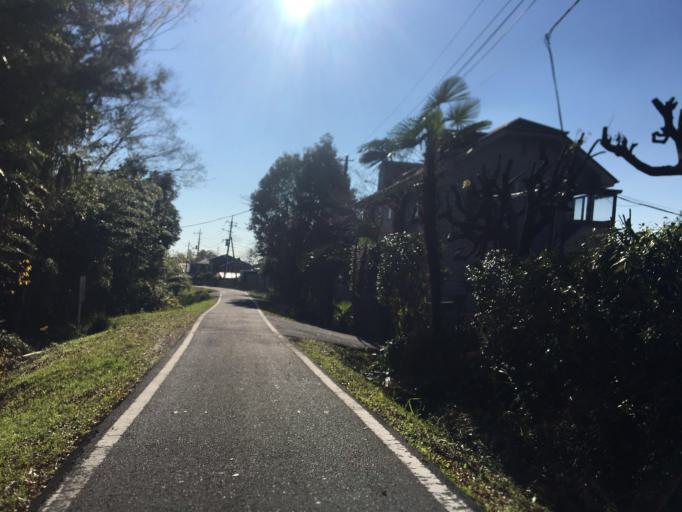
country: JP
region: Saitama
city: Yashio-shi
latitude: 35.8389
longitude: 139.8406
